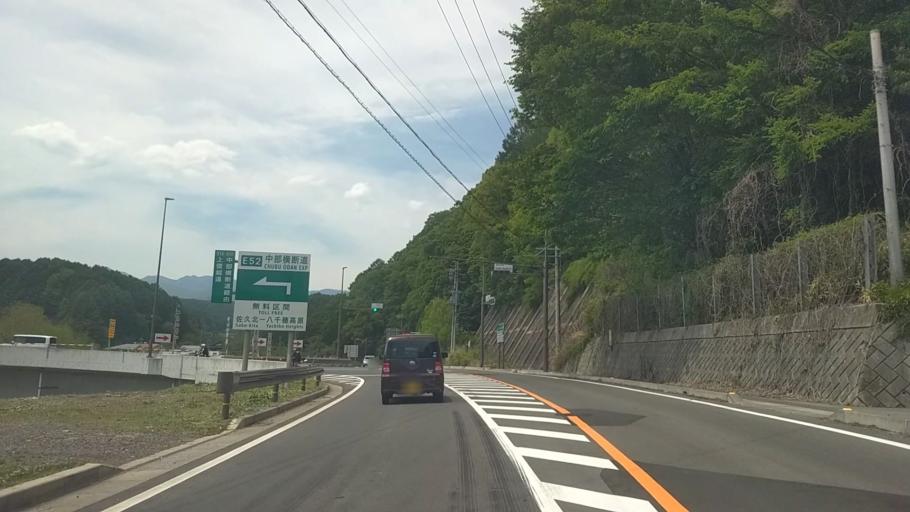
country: JP
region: Nagano
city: Saku
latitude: 36.1288
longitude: 138.4608
